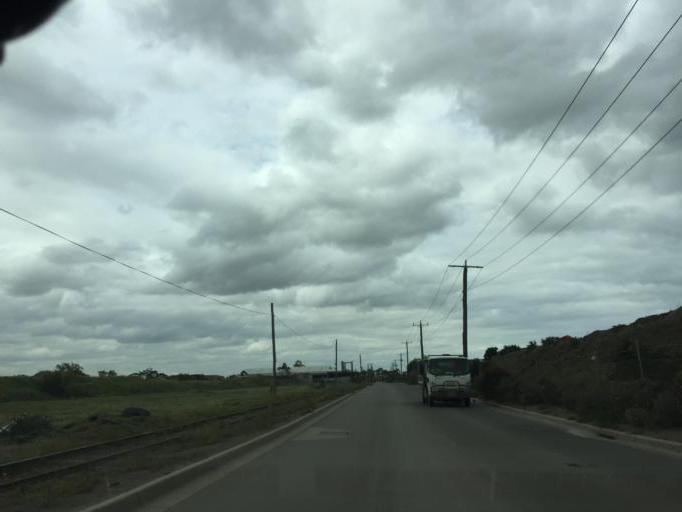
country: AU
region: Victoria
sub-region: Brimbank
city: Brooklyn
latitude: -37.8113
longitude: 144.8426
